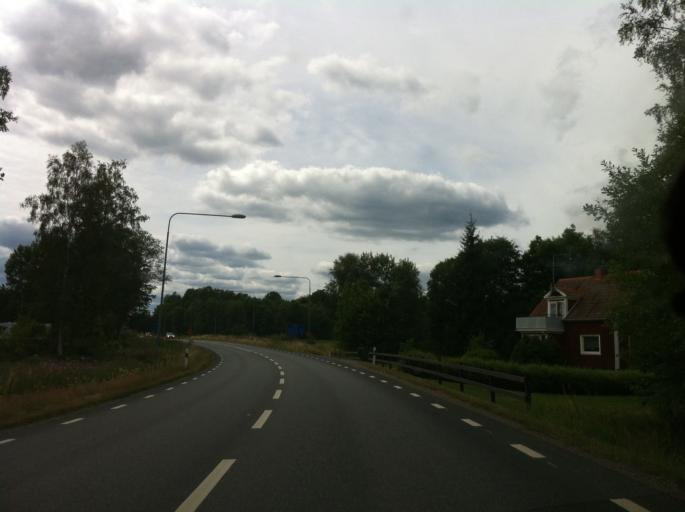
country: SE
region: Kronoberg
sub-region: Tingsryds Kommun
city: Tingsryd
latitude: 56.5296
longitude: 14.9602
